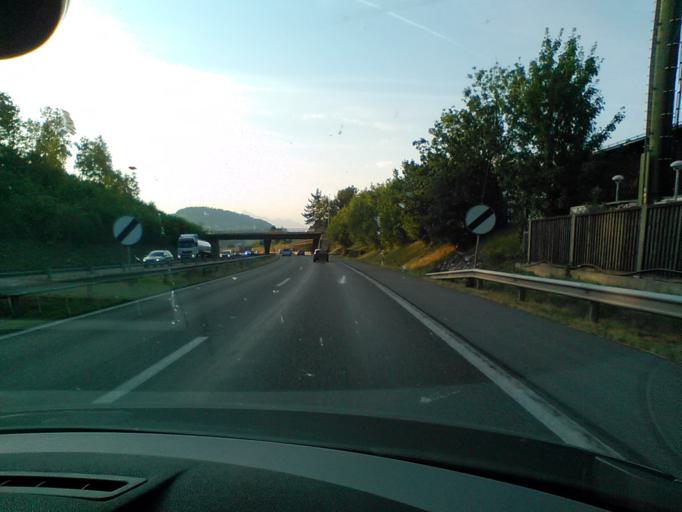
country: CH
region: Vaud
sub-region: Lavaux-Oron District
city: Belmont-sur-Lausanne
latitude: 46.5195
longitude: 6.6844
